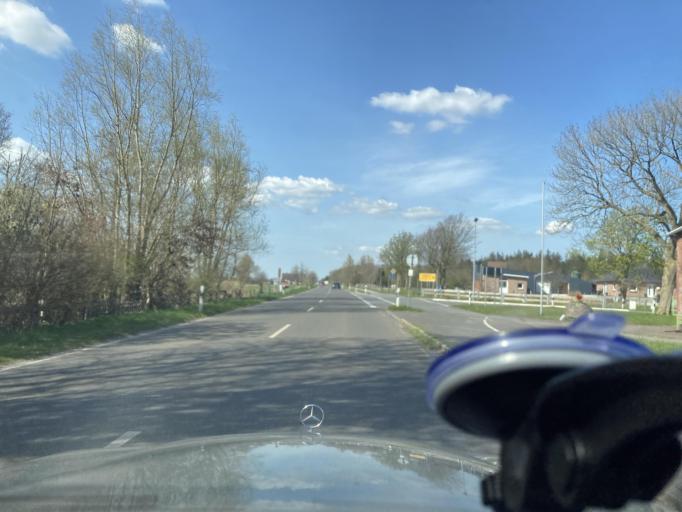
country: DE
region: Schleswig-Holstein
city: Krempel
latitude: 54.3078
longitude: 9.0348
